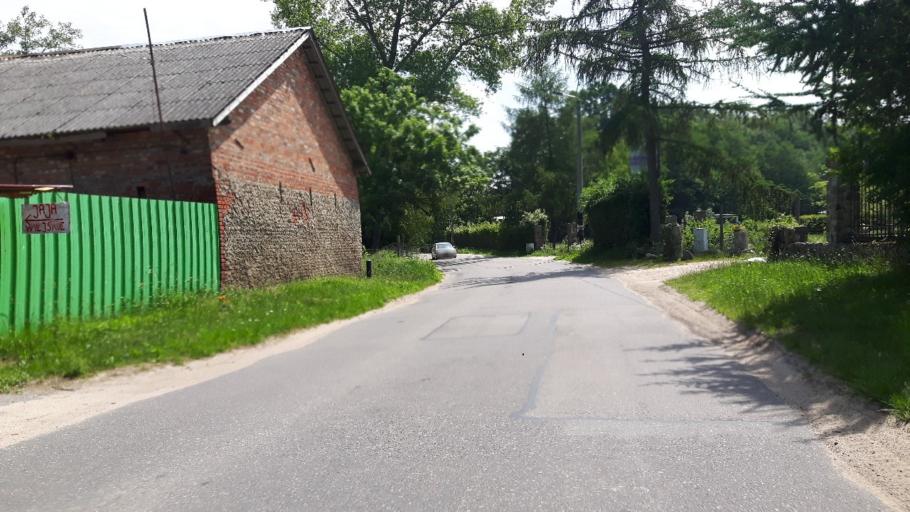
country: PL
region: Pomeranian Voivodeship
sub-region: Powiat wejherowski
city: Choczewo
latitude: 54.7558
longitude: 17.7896
